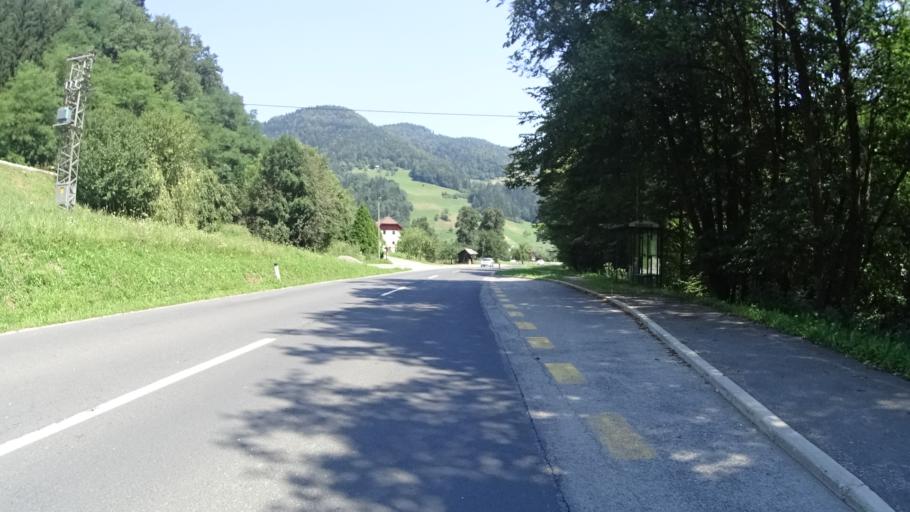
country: SI
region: Ravne na Koroskem
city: Ravne na Koroskem
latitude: 46.5496
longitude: 14.9830
